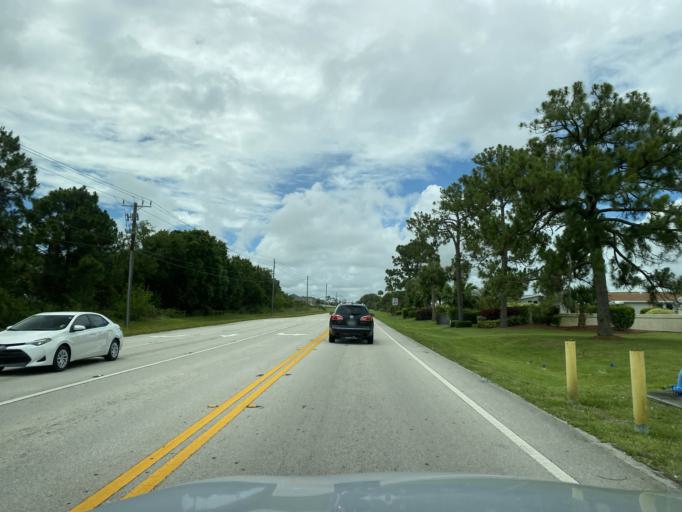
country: US
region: Florida
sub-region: Brevard County
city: West Melbourne
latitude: 28.0495
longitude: -80.6543
